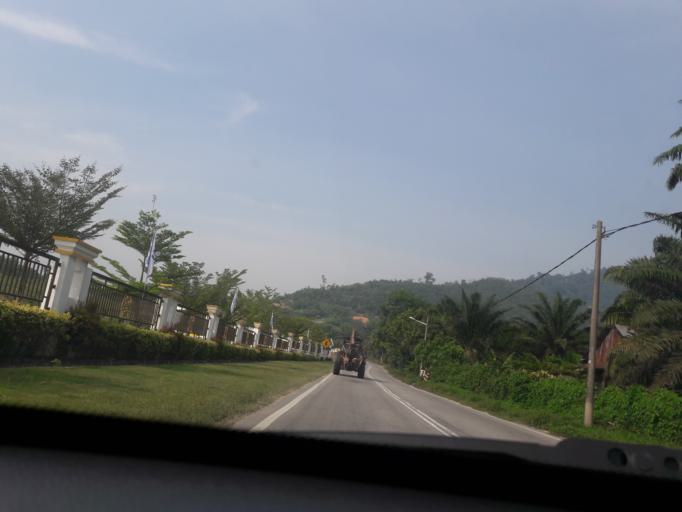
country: MY
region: Kedah
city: Kulim
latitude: 5.3744
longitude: 100.5216
